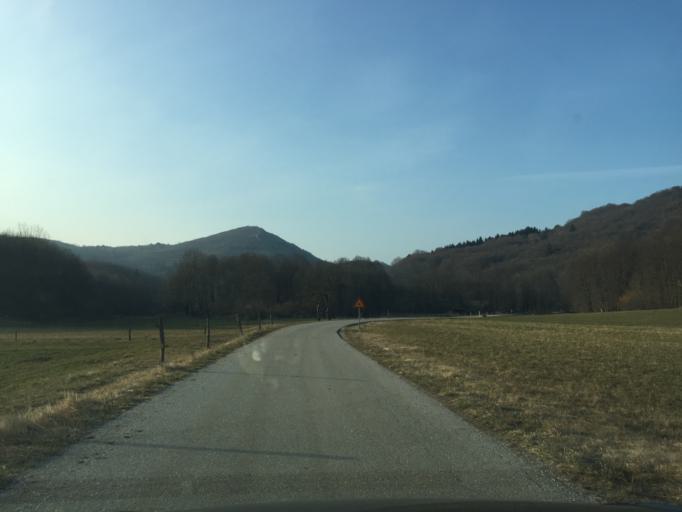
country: SI
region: Kanal
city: Kanal
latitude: 46.0476
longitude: 13.6752
